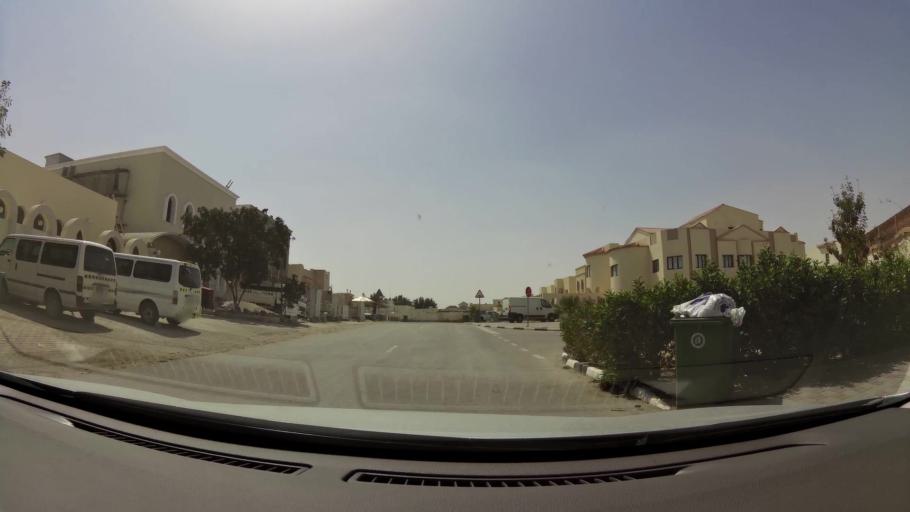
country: QA
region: Baladiyat Umm Salal
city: Umm Salal Muhammad
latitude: 25.3836
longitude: 51.4198
